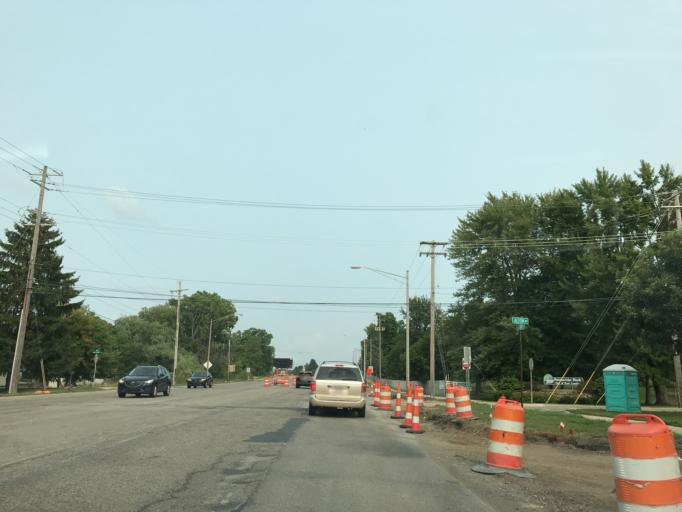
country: US
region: Michigan
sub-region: Ingham County
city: East Lansing
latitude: 42.7468
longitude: -84.4726
